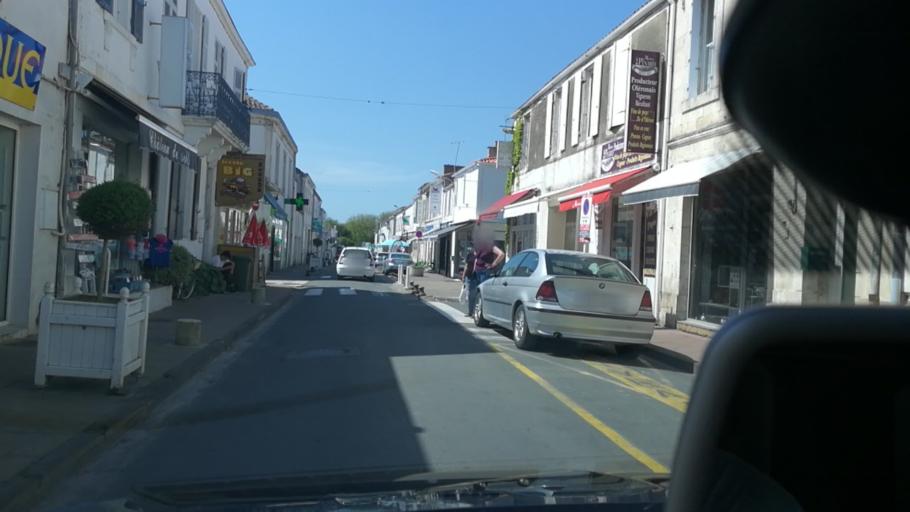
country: FR
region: Poitou-Charentes
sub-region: Departement de la Charente-Maritime
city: Saint-Trojan-les-Bains
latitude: 45.8869
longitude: -1.1960
